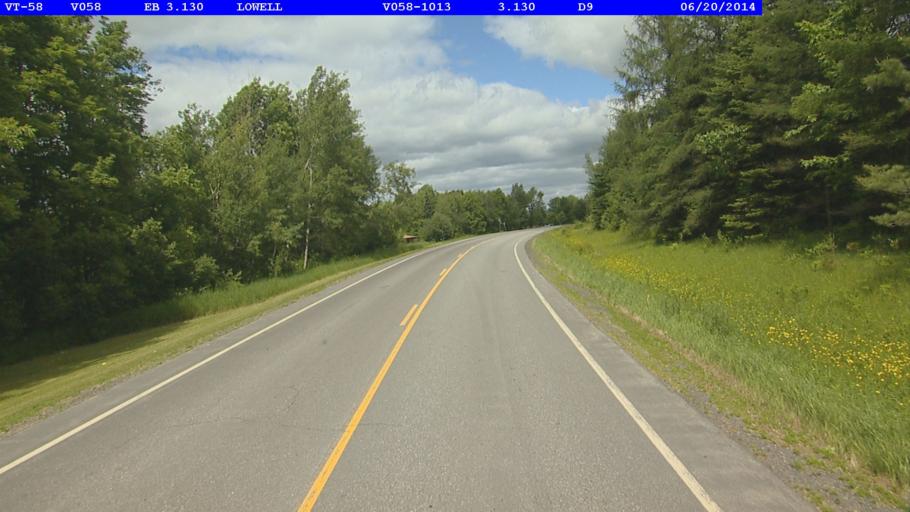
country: US
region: Vermont
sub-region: Orleans County
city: Newport
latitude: 44.8150
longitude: -72.3962
